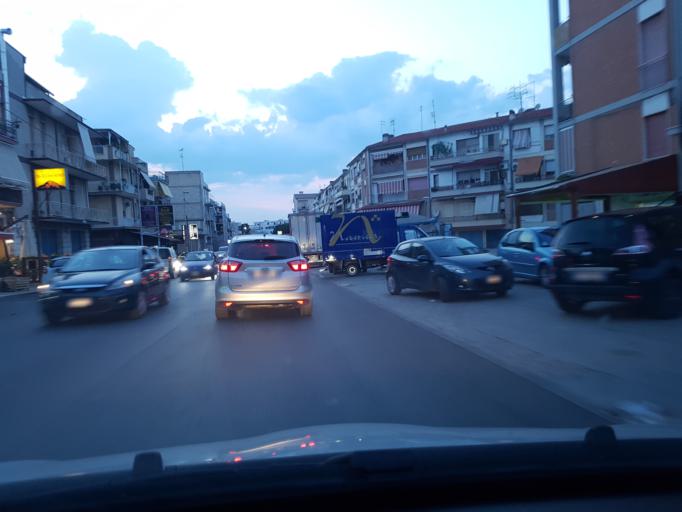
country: IT
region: Apulia
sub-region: Provincia di Foggia
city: Cerignola
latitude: 41.2607
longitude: 15.8912
